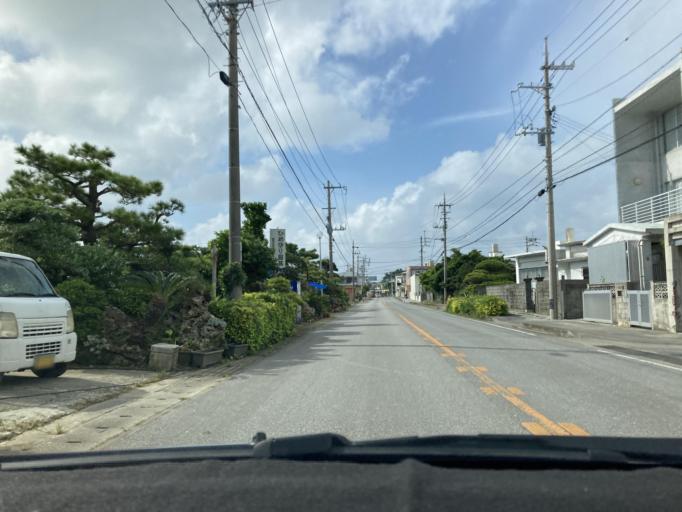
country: JP
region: Okinawa
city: Itoman
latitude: 26.1038
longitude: 127.6683
